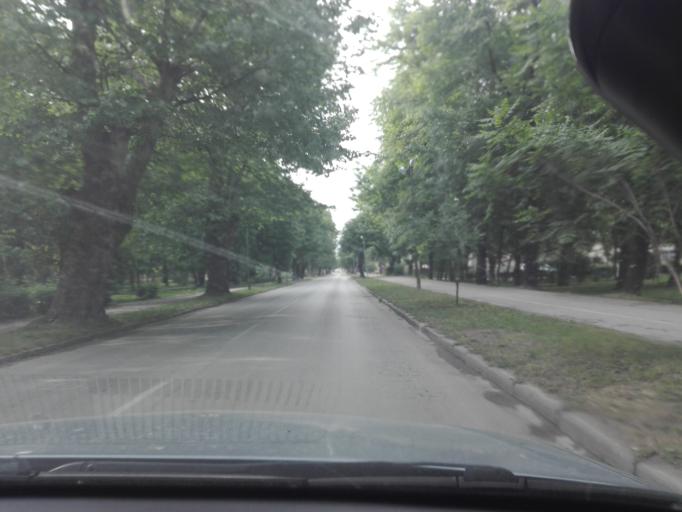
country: MK
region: Bitola
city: Bitola
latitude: 41.0201
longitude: 21.3411
